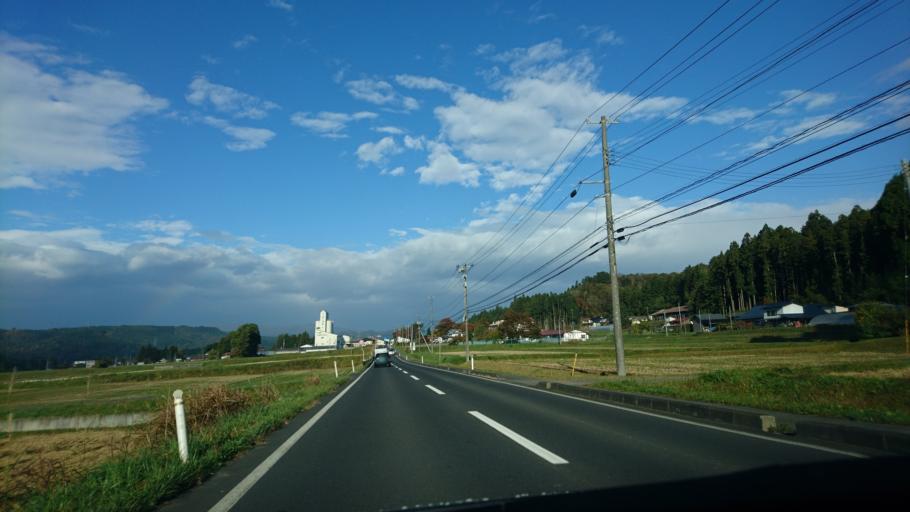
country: JP
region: Iwate
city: Ichinoseki
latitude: 39.0176
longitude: 141.0990
